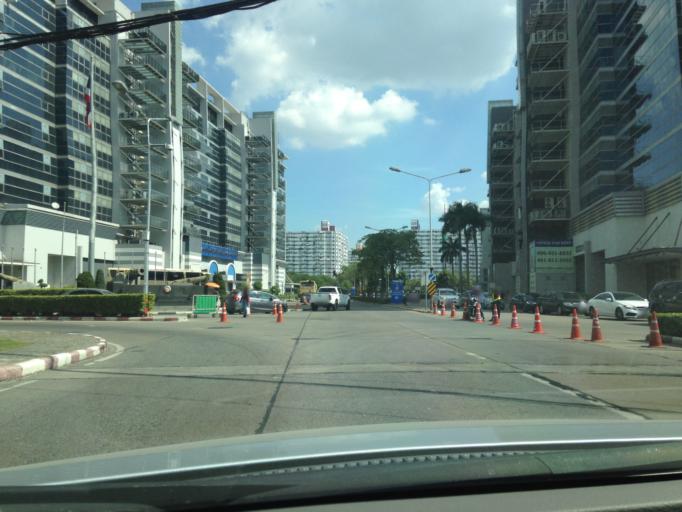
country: TH
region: Bangkok
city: Lak Si
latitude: 13.9103
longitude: 100.5487
